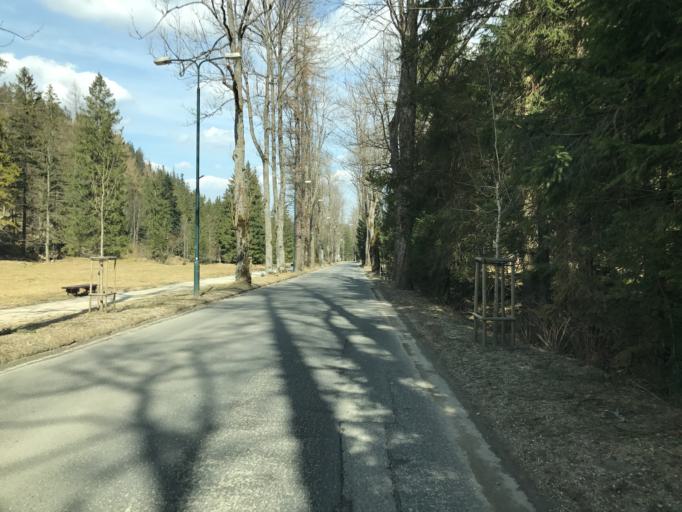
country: PL
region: Lesser Poland Voivodeship
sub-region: Powiat tatrzanski
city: Zakopane
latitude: 49.2752
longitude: 19.9809
